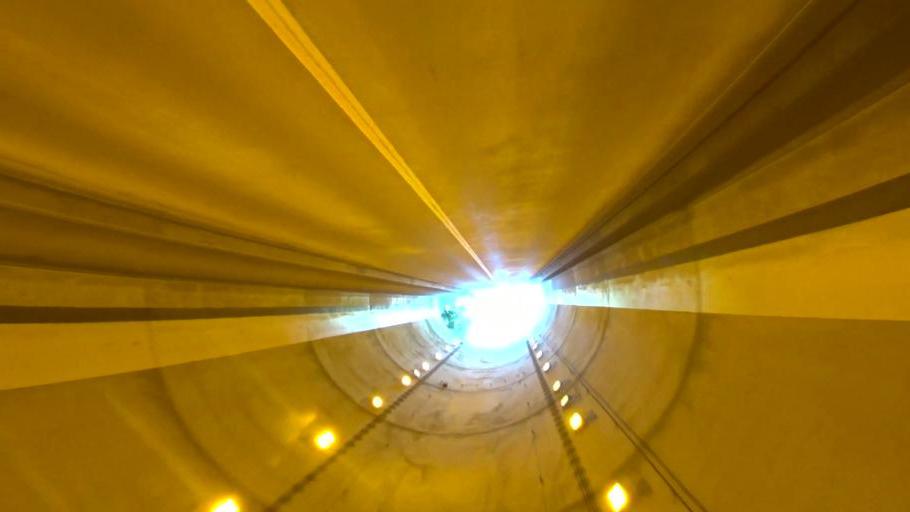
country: JP
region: Kyoto
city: Miyazu
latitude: 35.6631
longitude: 135.2603
